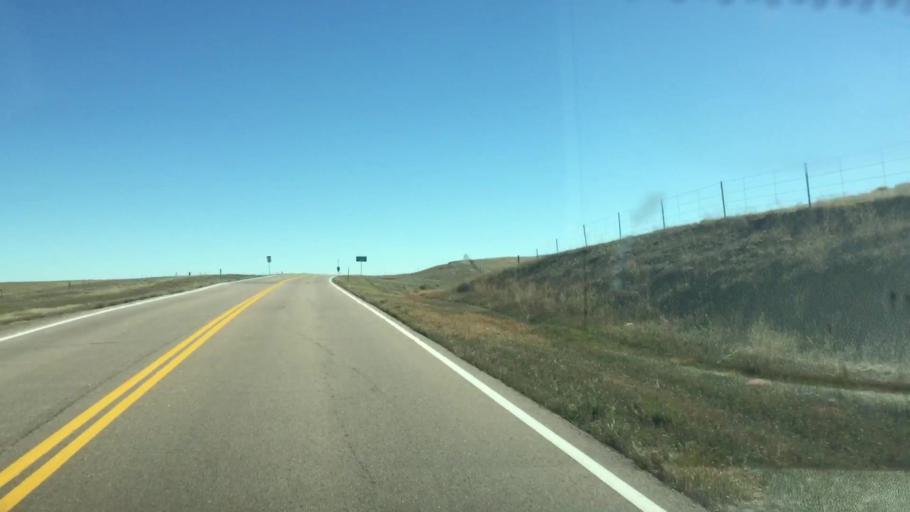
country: US
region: Colorado
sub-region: Lincoln County
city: Limon
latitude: 39.2868
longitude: -103.9777
